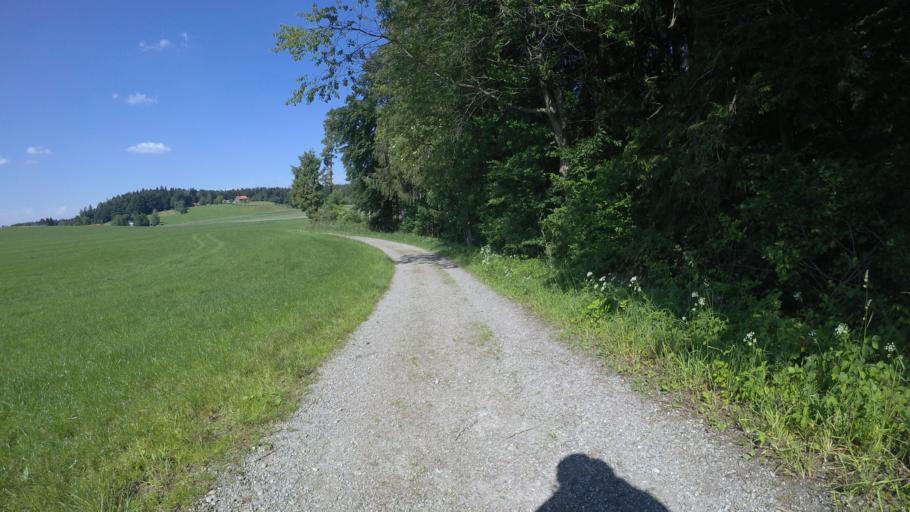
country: DE
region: Bavaria
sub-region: Upper Bavaria
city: Seeon-Seebruck
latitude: 47.9555
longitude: 12.5080
